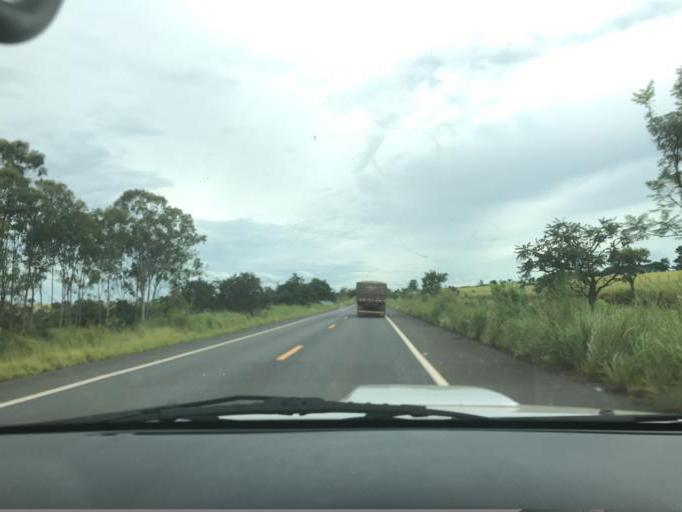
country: BR
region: Minas Gerais
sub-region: Araxa
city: Araxa
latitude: -19.3764
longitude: -46.8578
